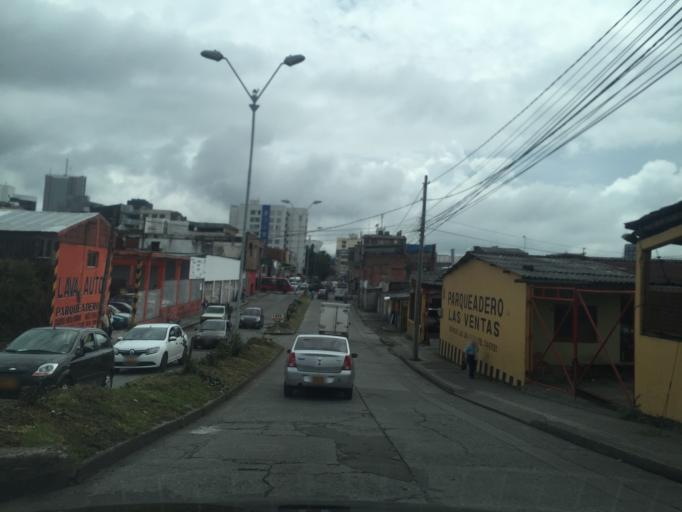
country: CO
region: Quindio
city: Armenia
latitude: 4.5349
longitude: -75.6774
